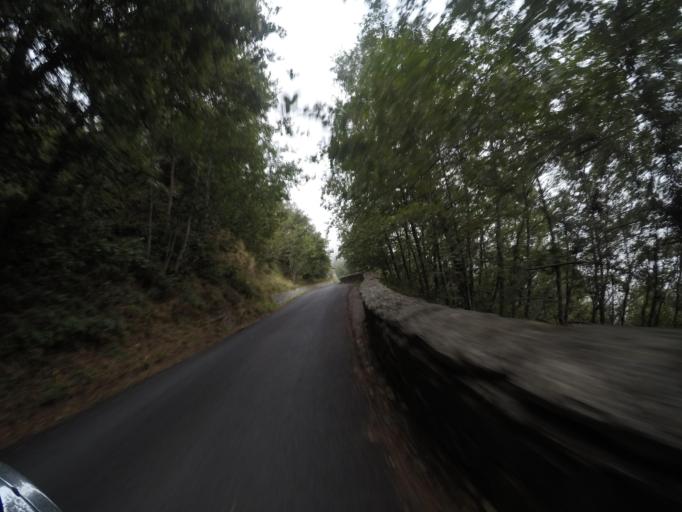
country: IT
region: Tuscany
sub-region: Provincia di Massa-Carrara
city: Carrara
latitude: 44.1141
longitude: 10.1203
